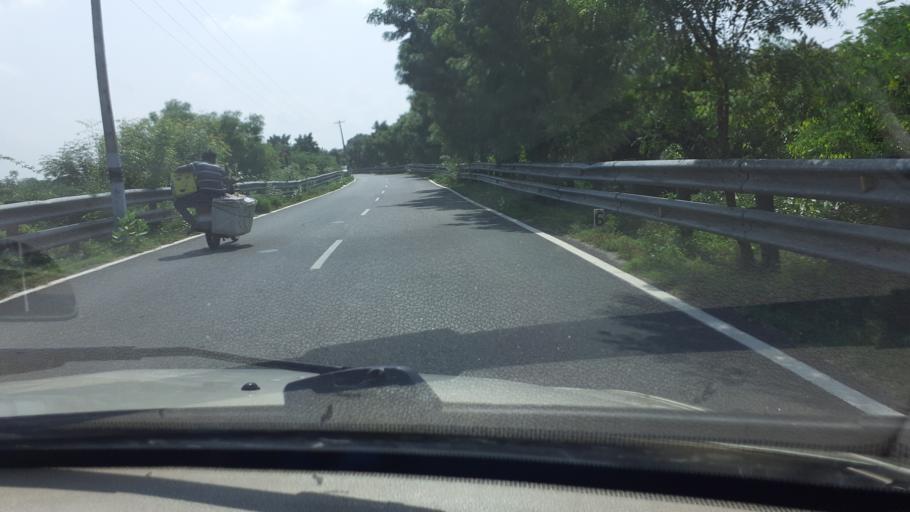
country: IN
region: Tamil Nadu
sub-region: Thoothukkudi
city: Srivaikuntam
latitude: 8.6188
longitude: 77.9125
